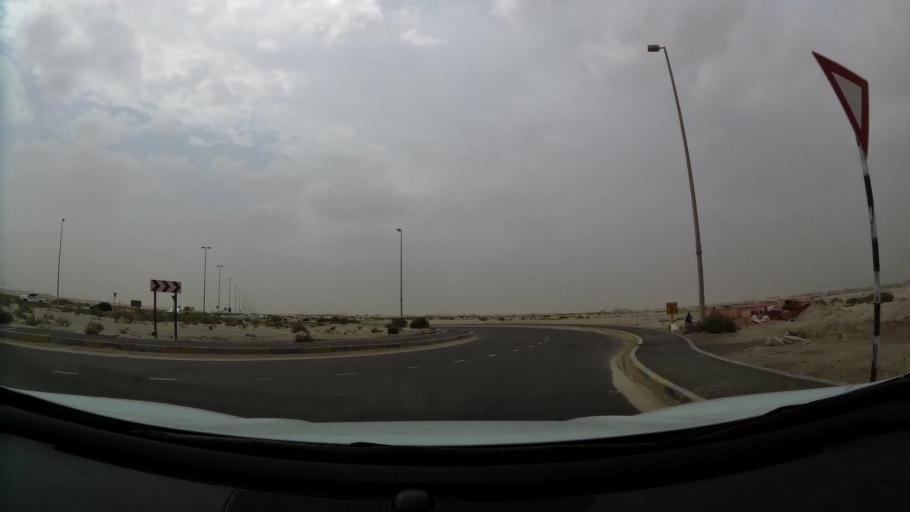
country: AE
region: Abu Dhabi
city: Abu Dhabi
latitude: 24.3868
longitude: 54.6796
